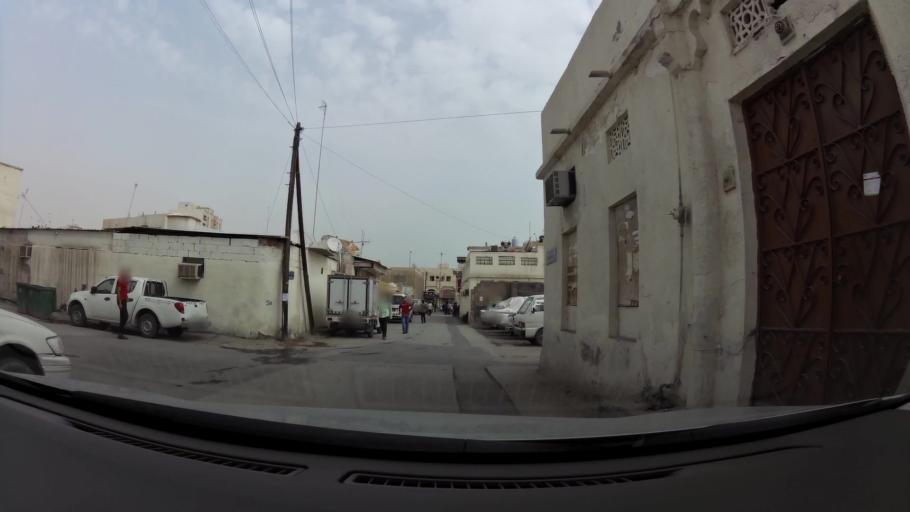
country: QA
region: Baladiyat ad Dawhah
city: Doha
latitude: 25.2686
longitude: 51.5396
